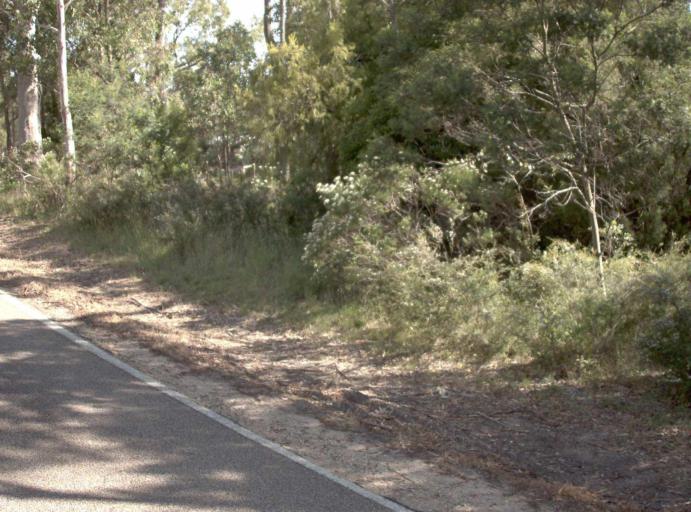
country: AU
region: Victoria
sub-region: East Gippsland
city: Lakes Entrance
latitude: -37.7783
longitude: 147.8205
